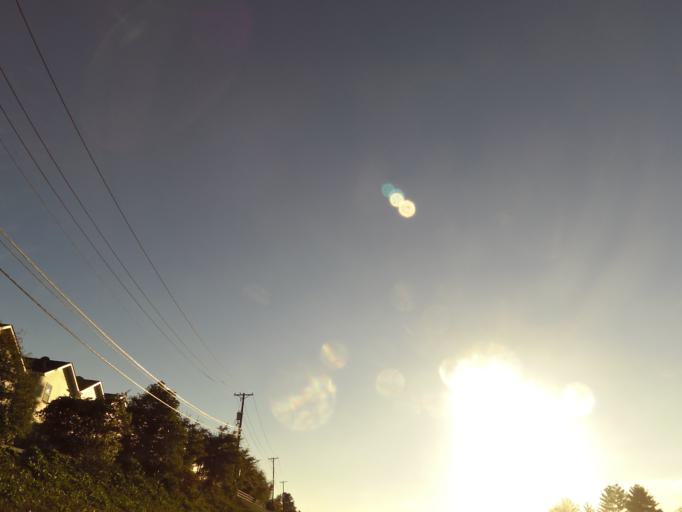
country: US
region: Tennessee
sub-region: Knox County
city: Knoxville
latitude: 36.0223
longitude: -84.0270
